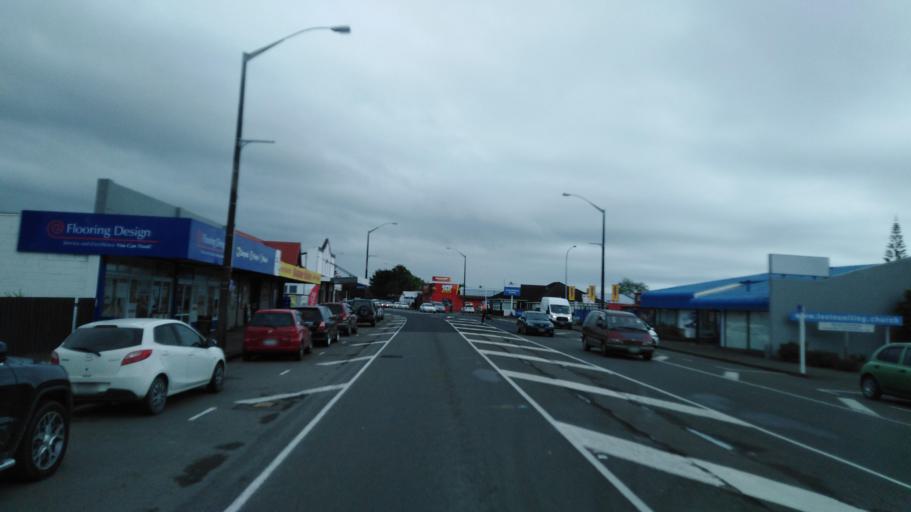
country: NZ
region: Manawatu-Wanganui
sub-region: Horowhenua District
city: Levin
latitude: -40.6267
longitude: 175.2817
